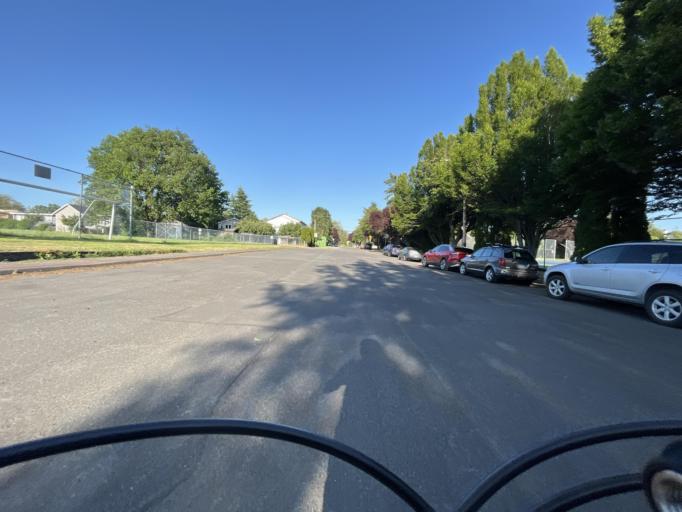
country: CA
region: British Columbia
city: Victoria
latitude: 48.4381
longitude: -123.3364
